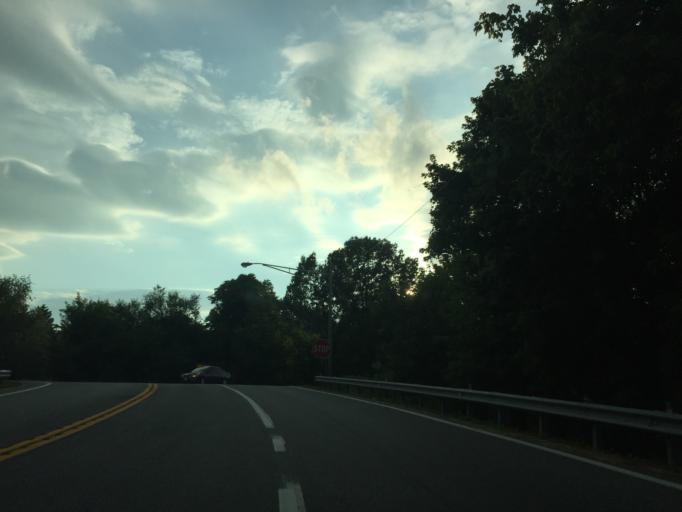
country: US
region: Maryland
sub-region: Harford County
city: Jarrettsville
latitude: 39.5901
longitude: -76.5086
